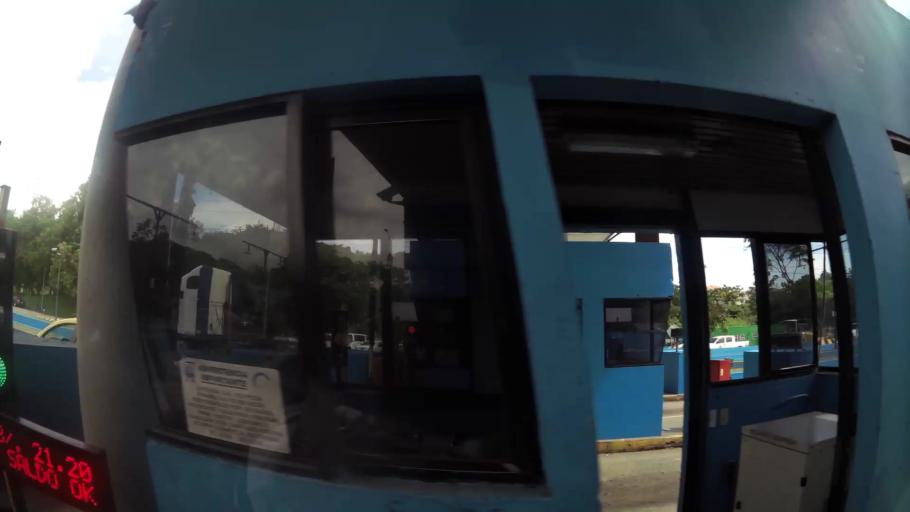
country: PA
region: Panama
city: Las Cumbres
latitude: 9.0486
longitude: -79.5284
